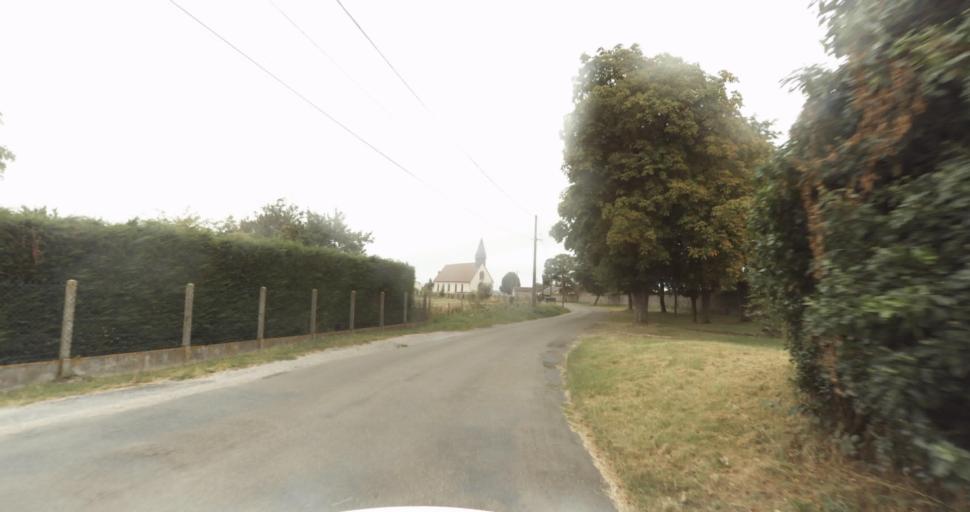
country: FR
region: Centre
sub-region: Departement d'Eure-et-Loir
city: Vert-en-Drouais
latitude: 48.7710
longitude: 1.2907
